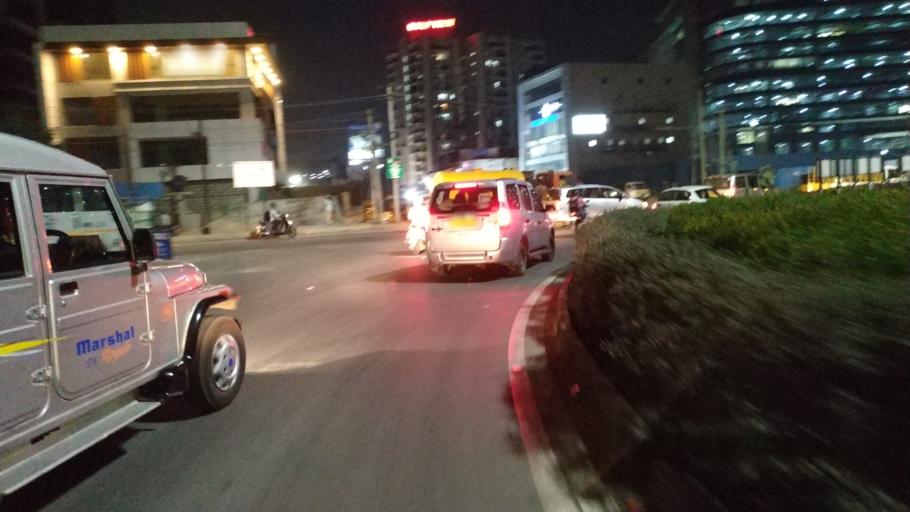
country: IN
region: Telangana
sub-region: Rangareddi
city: Kukatpalli
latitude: 17.4192
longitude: 78.3551
